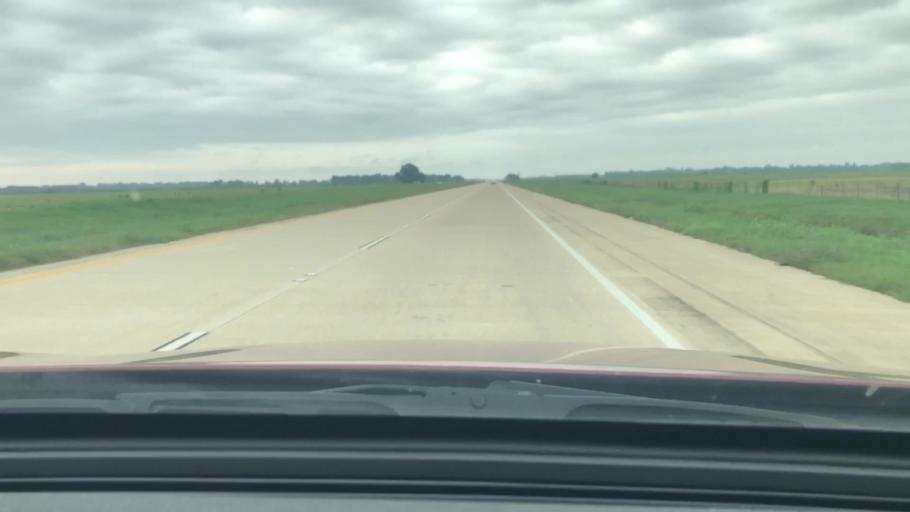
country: US
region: Louisiana
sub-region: Caddo Parish
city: Oil City
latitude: 32.7366
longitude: -93.8762
